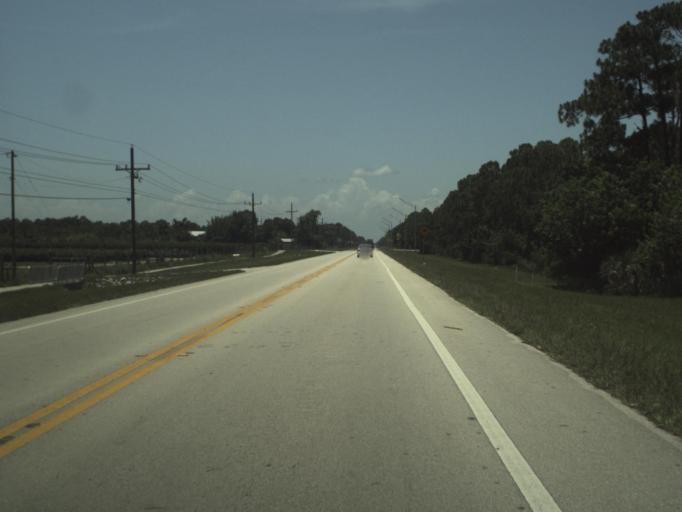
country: US
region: Florida
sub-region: Martin County
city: Palm City
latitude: 27.1616
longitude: -80.3309
